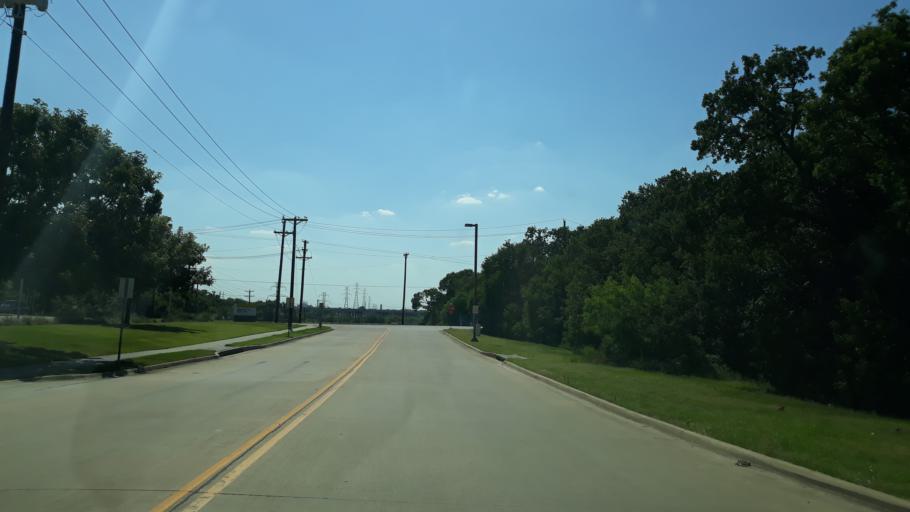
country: US
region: Texas
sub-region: Dallas County
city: Irving
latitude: 32.8173
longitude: -97.0071
